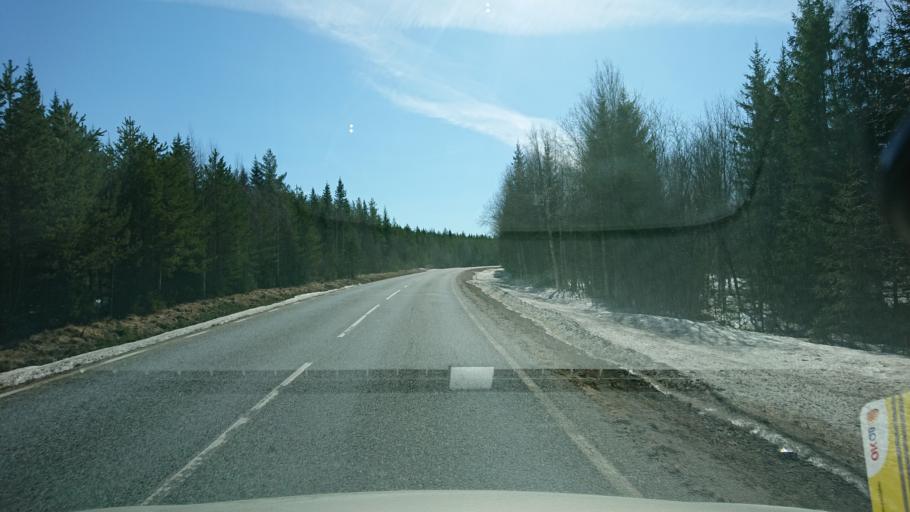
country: SE
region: Vaesterbotten
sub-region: Dorotea Kommun
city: Dorotea
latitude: 63.9942
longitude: 16.3135
